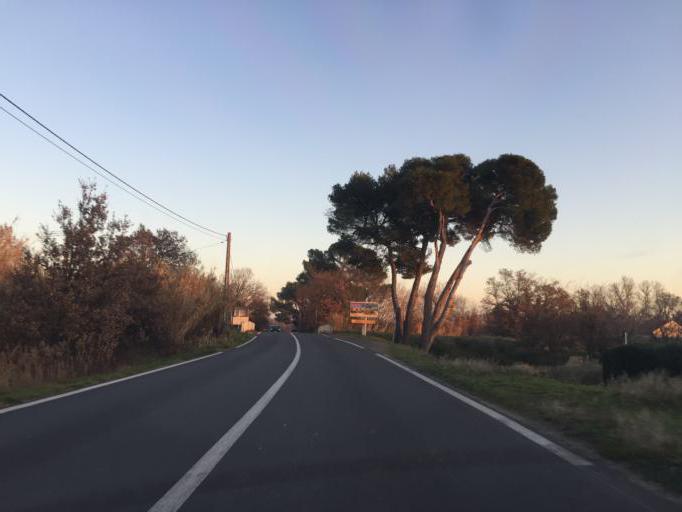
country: FR
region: Provence-Alpes-Cote d'Azur
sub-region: Departement du Vaucluse
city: Loriol-du-Comtat
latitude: 44.0793
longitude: 4.9857
